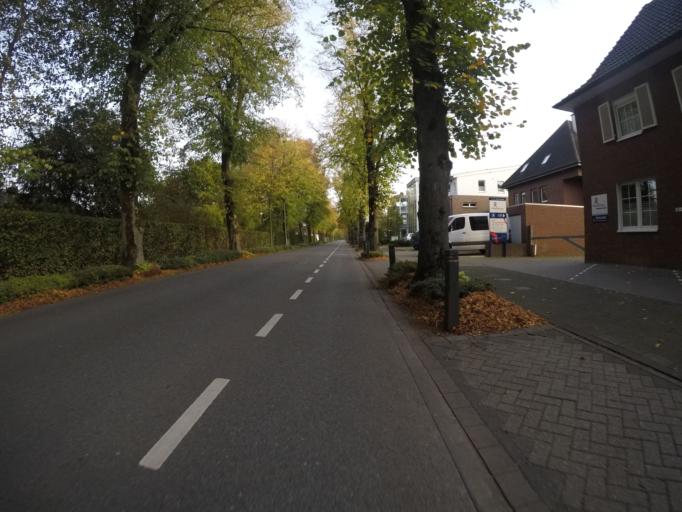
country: DE
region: North Rhine-Westphalia
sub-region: Regierungsbezirk Munster
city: Rhede
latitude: 51.8387
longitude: 6.7016
